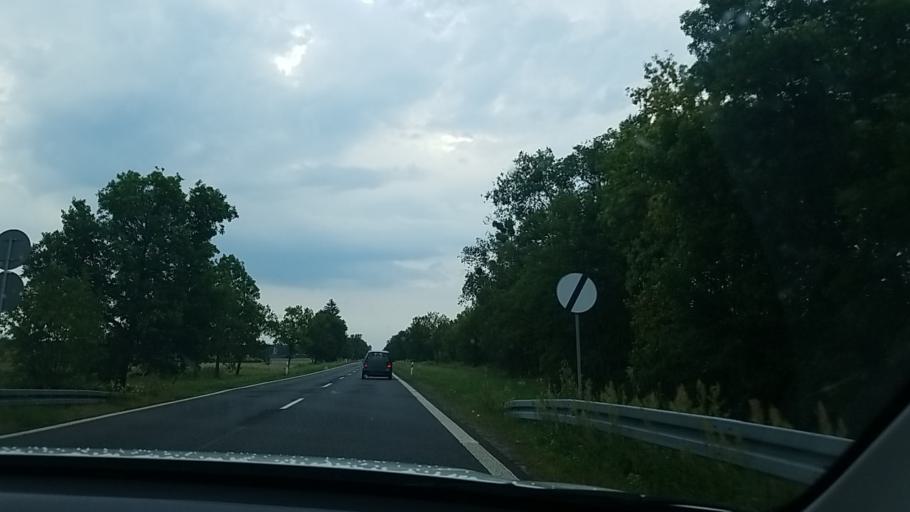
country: PL
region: Lublin Voivodeship
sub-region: Powiat wlodawski
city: Hansk
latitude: 51.4646
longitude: 23.3135
